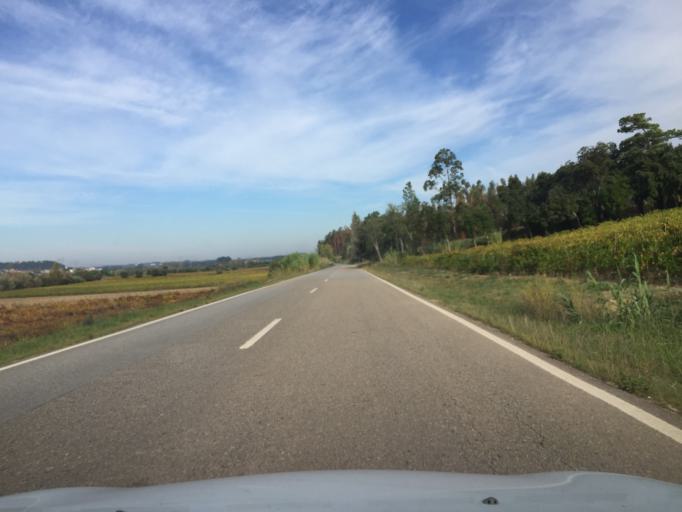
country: PT
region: Aveiro
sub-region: Anadia
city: Anadia
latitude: 40.4263
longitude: -8.4135
